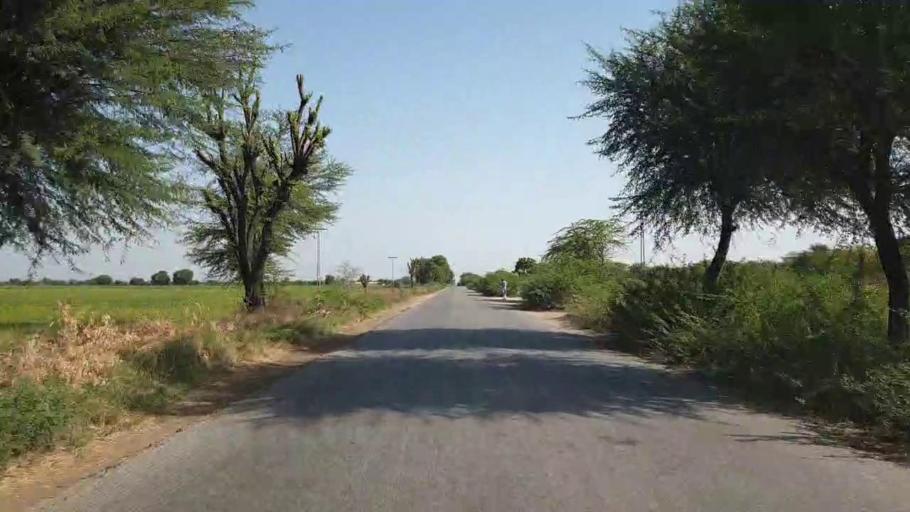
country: PK
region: Sindh
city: Chor
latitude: 25.4427
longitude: 69.7510
